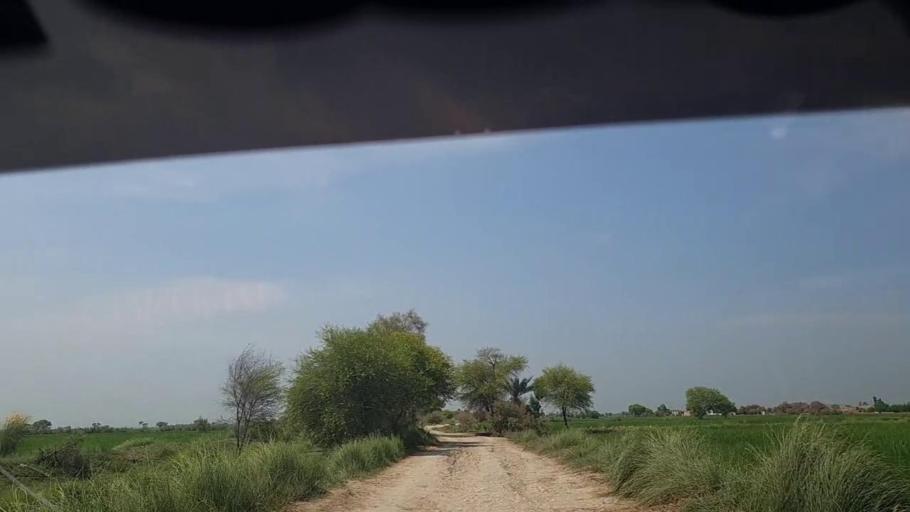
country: PK
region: Sindh
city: Thul
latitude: 28.1863
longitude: 68.7192
